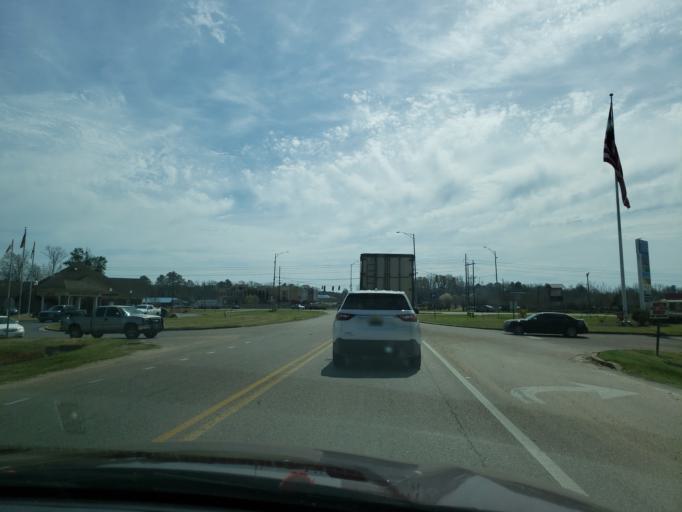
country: US
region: Alabama
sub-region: Dallas County
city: Selma
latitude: 32.4347
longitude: -87.0610
